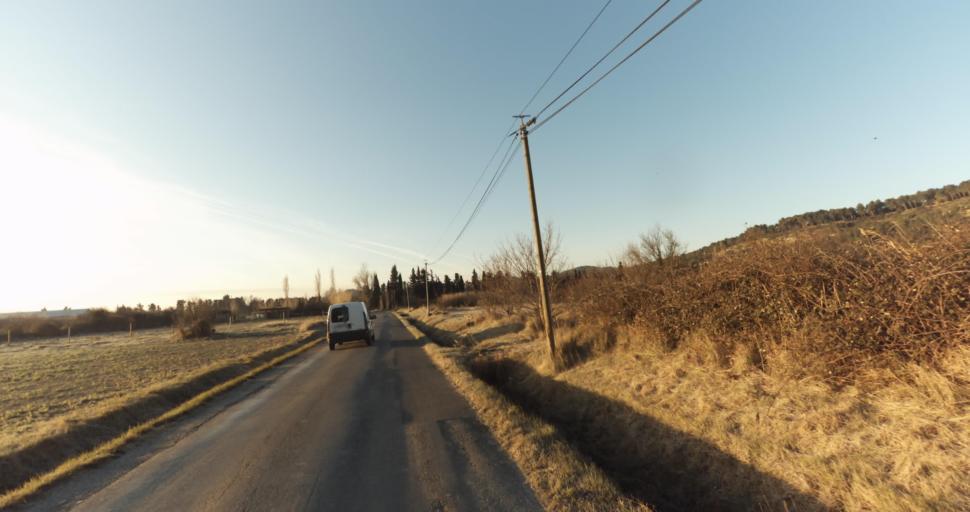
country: FR
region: Provence-Alpes-Cote d'Azur
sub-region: Departement des Bouches-du-Rhone
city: Barbentane
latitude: 43.8925
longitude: 4.7716
